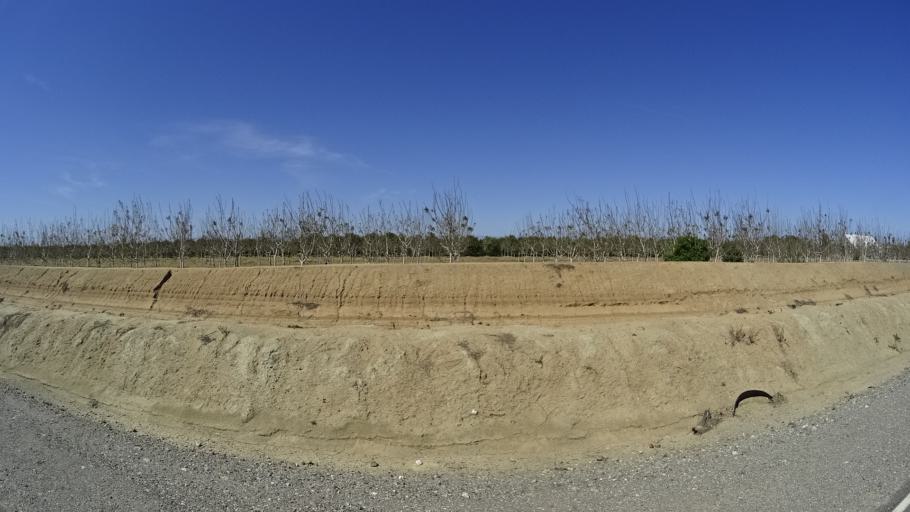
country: US
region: California
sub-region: Glenn County
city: Orland
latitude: 39.6979
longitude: -122.1403
